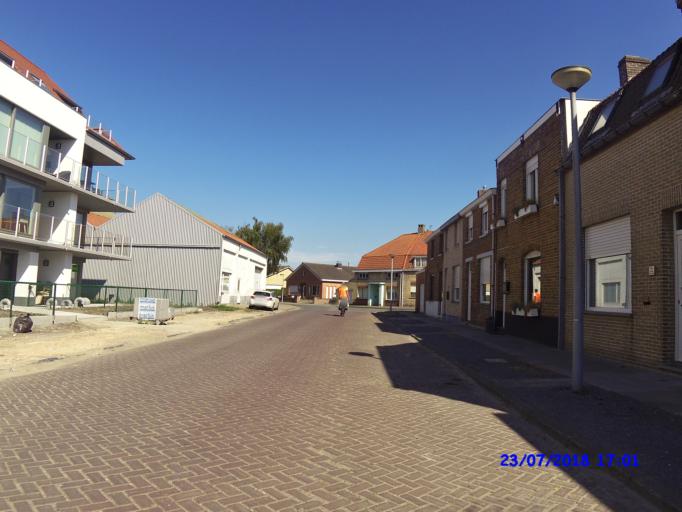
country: BE
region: Flanders
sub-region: Provincie West-Vlaanderen
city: Veurne
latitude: 51.0724
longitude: 2.6756
